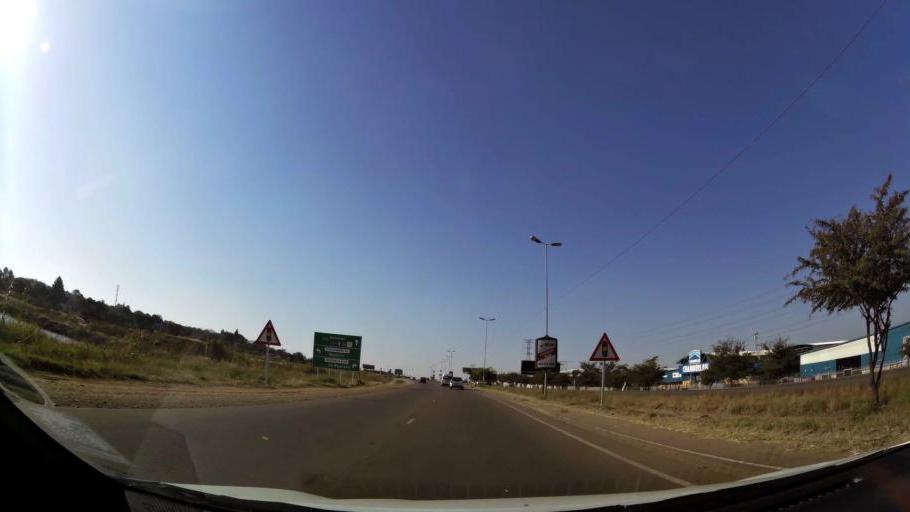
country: ZA
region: Gauteng
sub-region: City of Tshwane Metropolitan Municipality
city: Pretoria
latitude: -25.7732
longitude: 28.3520
